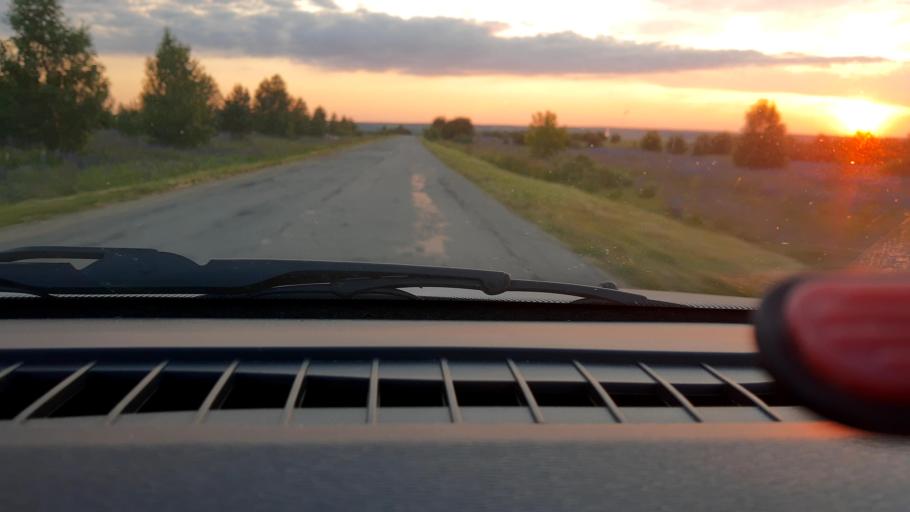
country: RU
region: Nizjnij Novgorod
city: Surovatikha
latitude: 55.8489
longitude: 43.9538
